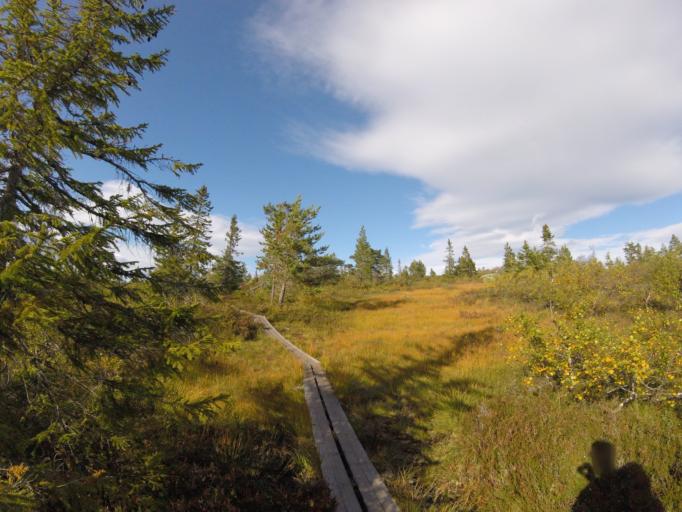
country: NO
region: Buskerud
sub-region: Flesberg
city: Lampeland
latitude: 59.7670
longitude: 9.4121
